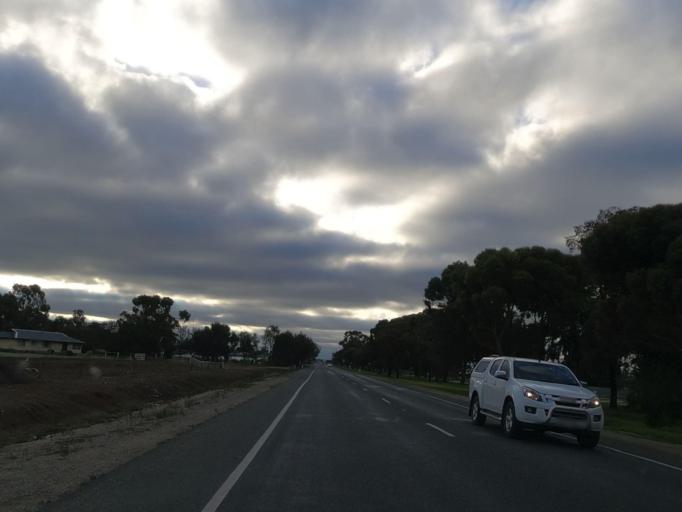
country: AU
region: Victoria
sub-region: Swan Hill
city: Swan Hill
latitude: -35.7440
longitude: 143.9214
